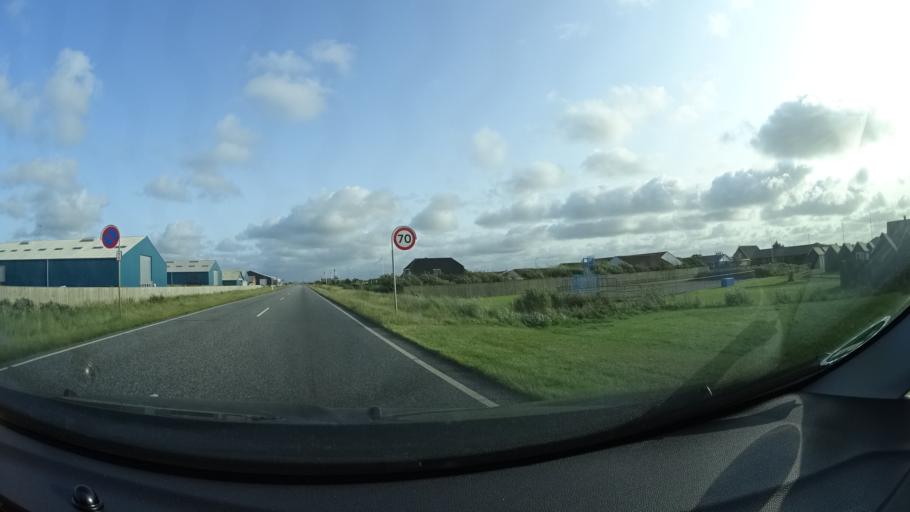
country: DK
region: Central Jutland
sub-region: Lemvig Kommune
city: Thyboron
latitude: 56.6976
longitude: 8.2160
